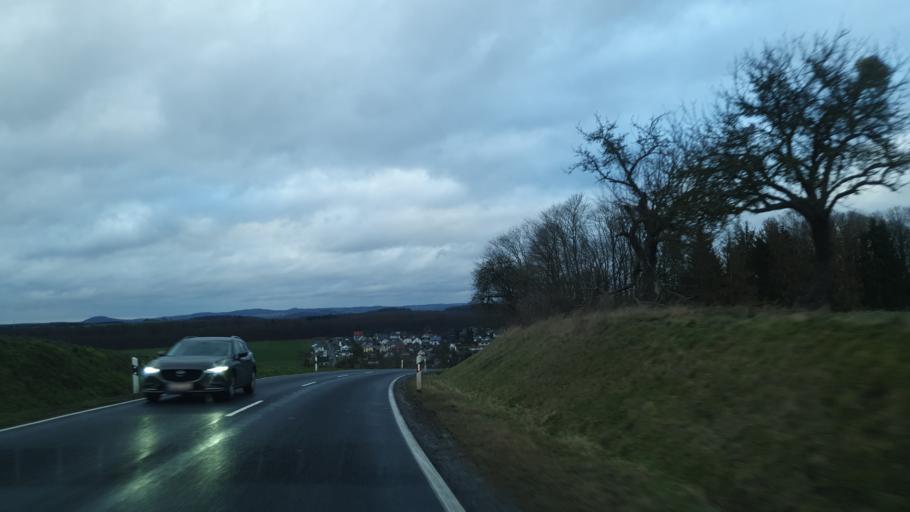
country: DE
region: Rheinland-Pfalz
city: Hirschberg
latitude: 50.3984
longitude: 7.9283
